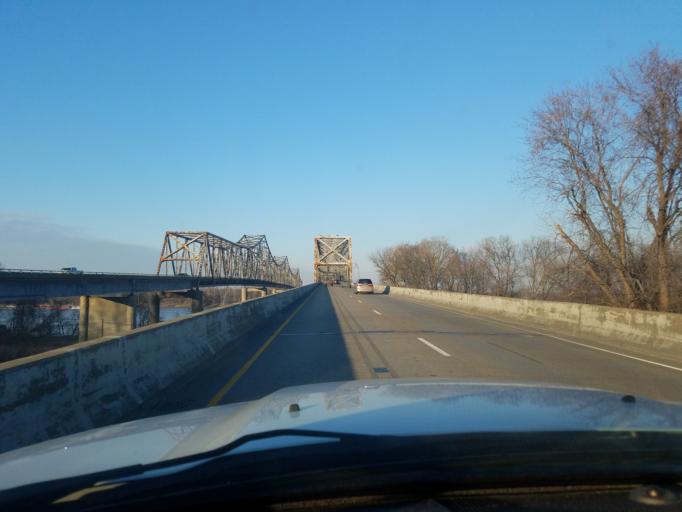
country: US
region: Indiana
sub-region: Vanderburgh County
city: Evansville
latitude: 37.9014
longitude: -87.5520
